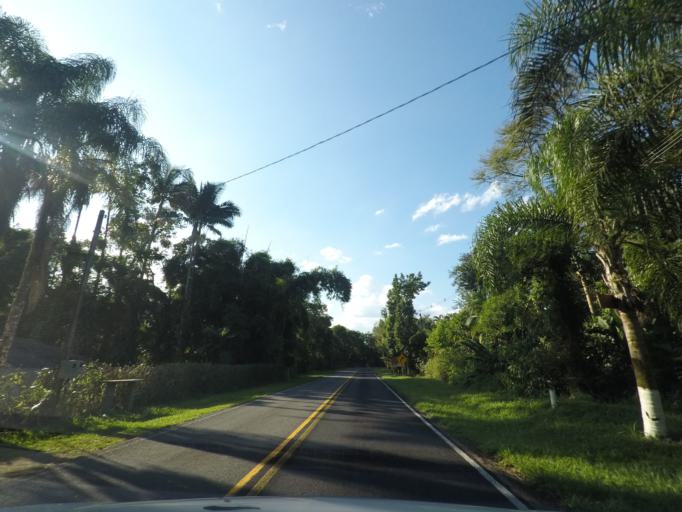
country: BR
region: Parana
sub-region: Antonina
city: Antonina
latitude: -25.4209
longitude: -48.8752
